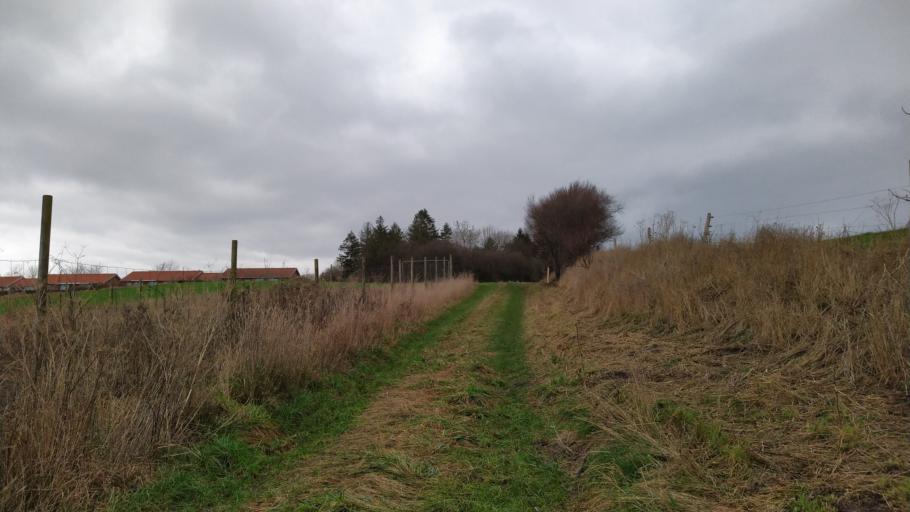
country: DK
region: Capital Region
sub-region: Egedal Kommune
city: Stenlose
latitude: 55.7631
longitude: 12.2082
